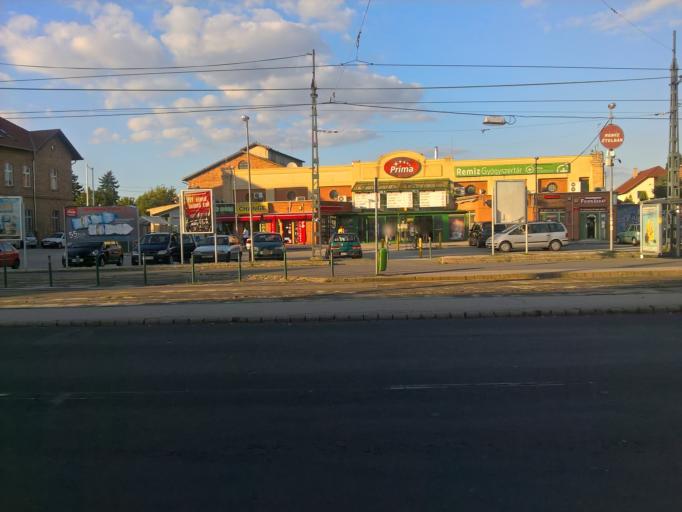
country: HU
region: Budapest
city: Budapest XIX. keruelet
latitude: 47.4525
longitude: 19.1564
